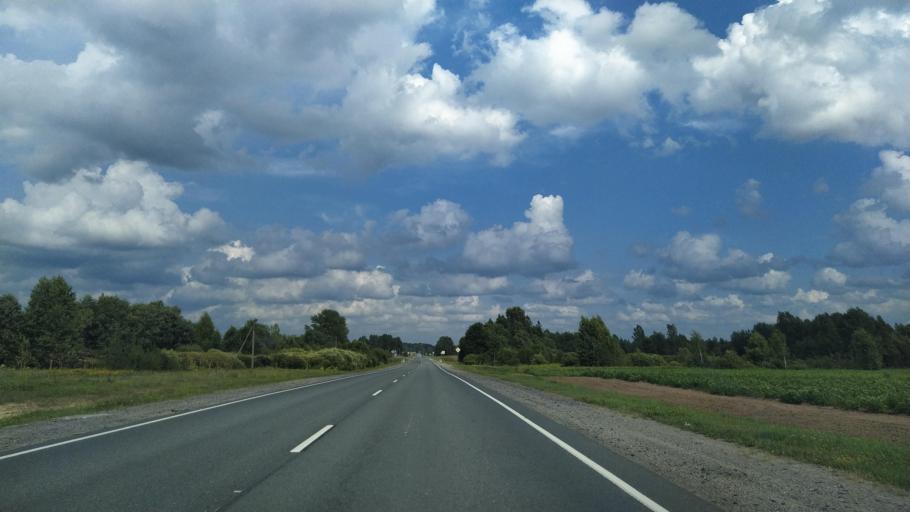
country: RU
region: Novgorod
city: Sol'tsy
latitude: 58.0973
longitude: 30.1799
